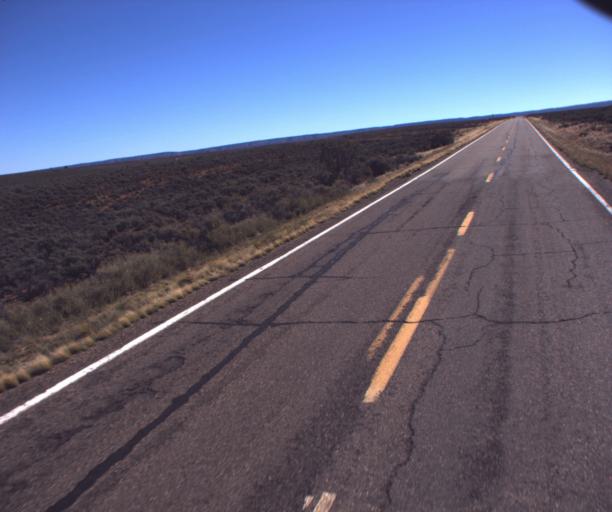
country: US
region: Arizona
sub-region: Coconino County
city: Fredonia
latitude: 36.9013
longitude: -112.3782
